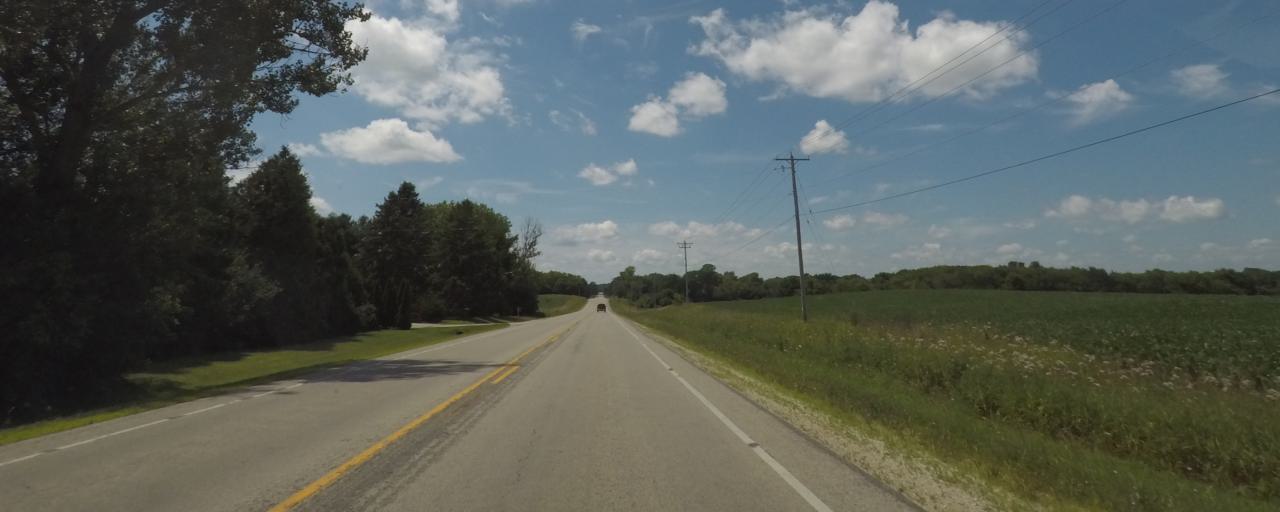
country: US
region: Wisconsin
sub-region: Jefferson County
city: Fort Atkinson
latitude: 42.9390
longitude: -88.7544
